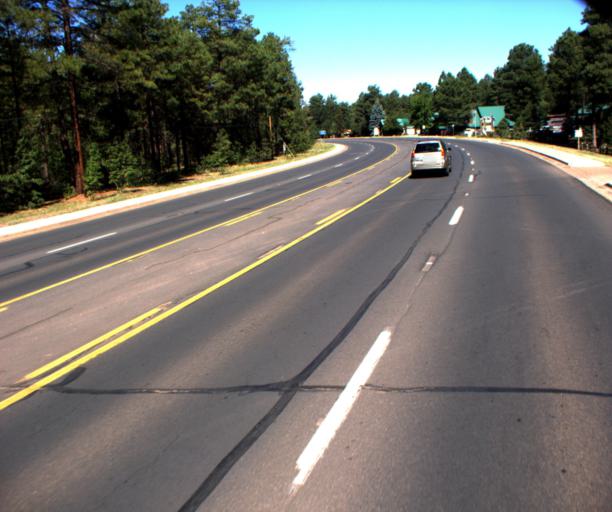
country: US
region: Arizona
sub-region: Navajo County
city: Pinetop-Lakeside
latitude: 34.1463
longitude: -109.9592
